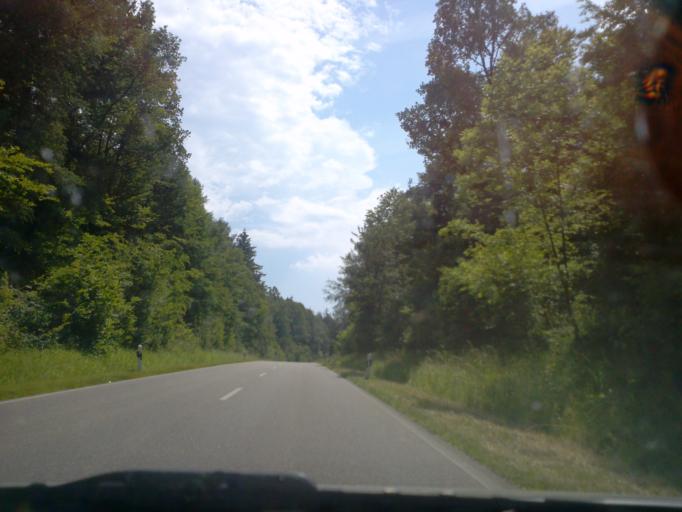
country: DE
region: Baden-Wuerttemberg
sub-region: Karlsruhe Region
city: Woessingen
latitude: 49.0006
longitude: 8.6334
